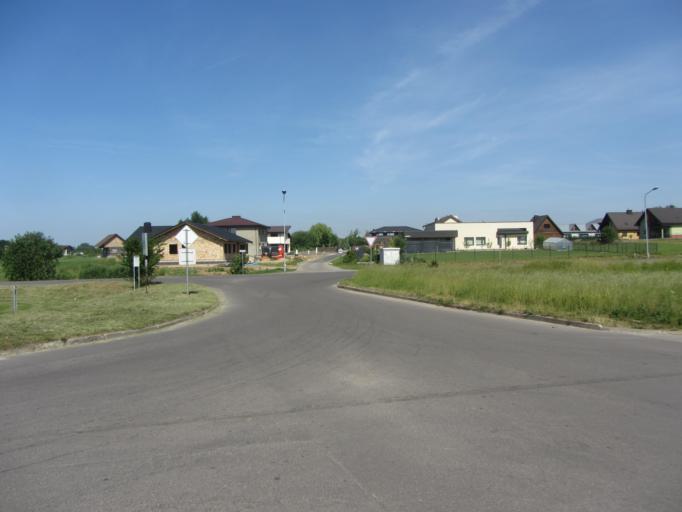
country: LT
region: Kauno apskritis
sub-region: Kauno rajonas
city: Karmelava
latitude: 54.8680
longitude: 24.2141
